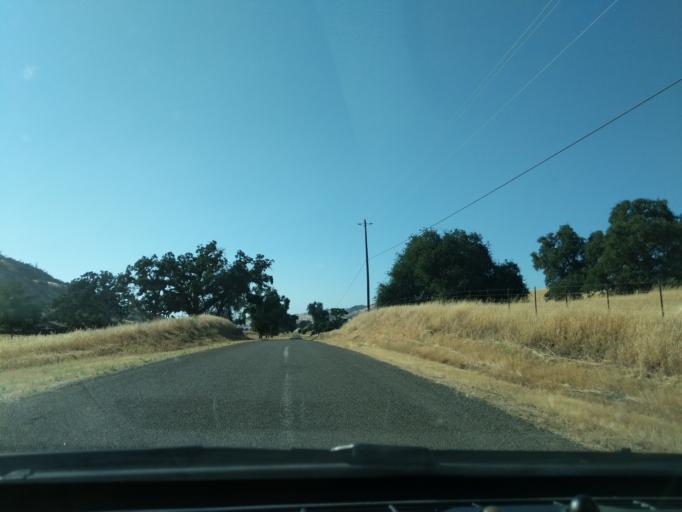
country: US
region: California
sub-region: San Luis Obispo County
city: San Miguel
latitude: 36.1326
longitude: -120.7455
